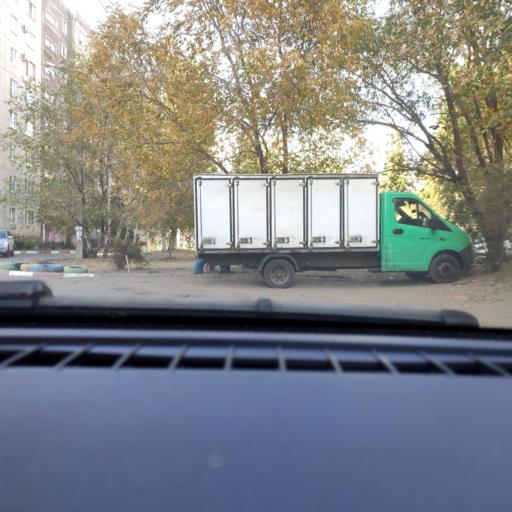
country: RU
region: Voronezj
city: Voronezh
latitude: 51.6730
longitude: 39.2459
